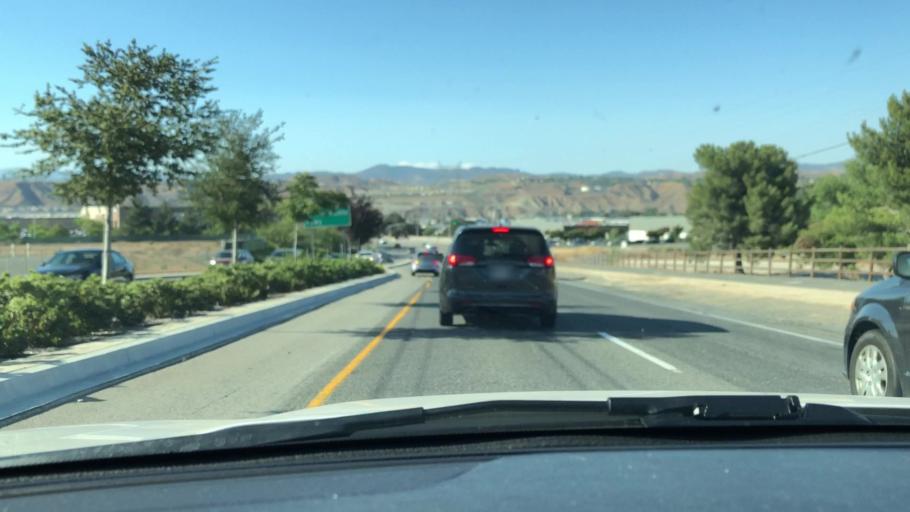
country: US
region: California
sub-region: Los Angeles County
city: Santa Clarita
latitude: 34.4108
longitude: -118.5027
